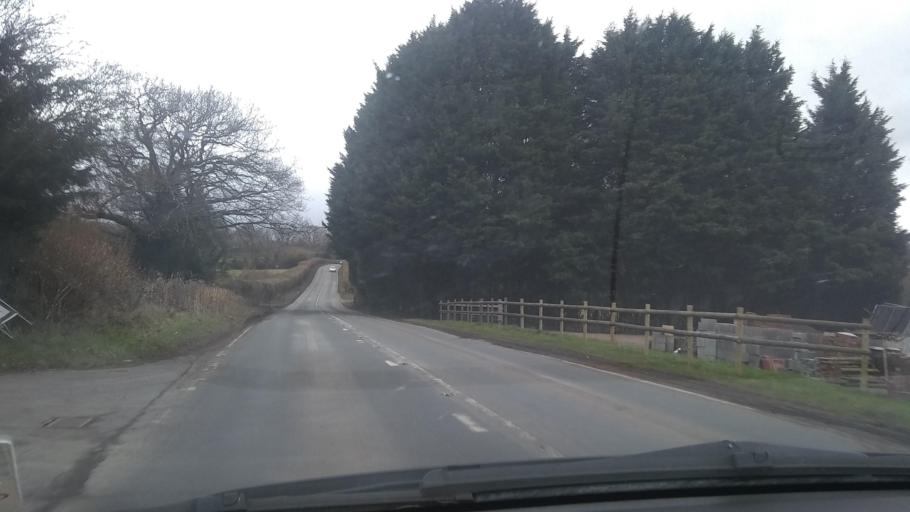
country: GB
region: England
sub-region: Shropshire
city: Cleobury Mortimer
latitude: 52.3740
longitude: -2.4135
